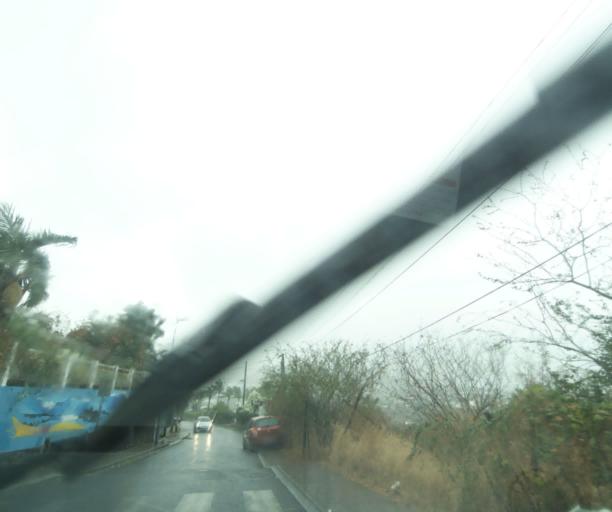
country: RE
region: Reunion
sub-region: Reunion
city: Saint-Paul
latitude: -21.0492
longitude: 55.2268
